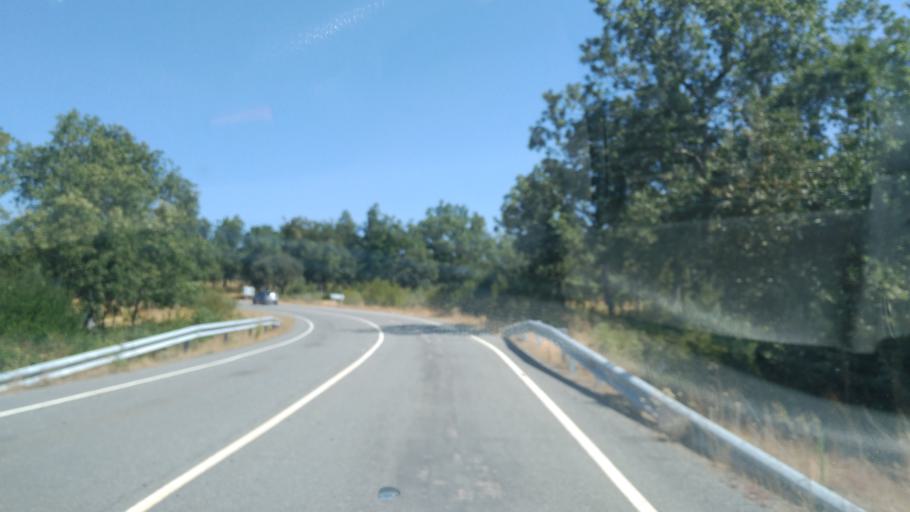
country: ES
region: Castille and Leon
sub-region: Provincia de Salamanca
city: Cereceda de la Sierra
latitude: 40.5903
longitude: -6.0887
